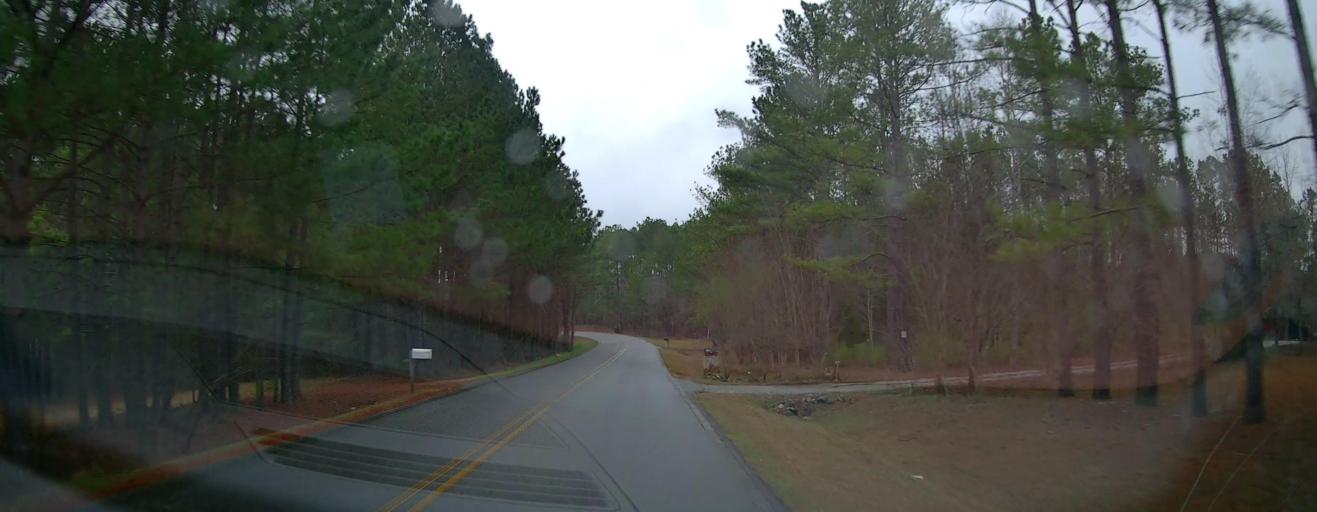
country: US
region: Georgia
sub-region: Monroe County
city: Forsyth
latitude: 33.0836
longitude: -83.9153
